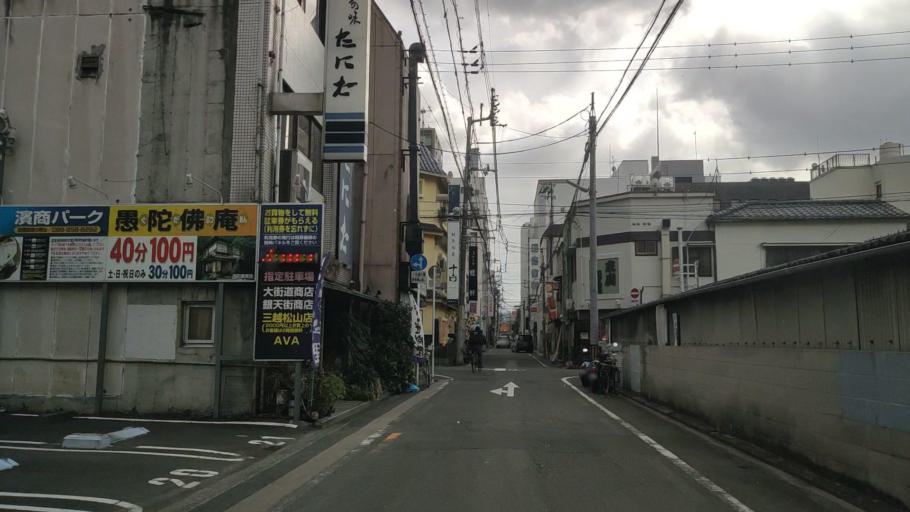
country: JP
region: Ehime
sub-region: Shikoku-chuo Shi
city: Matsuyama
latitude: 33.8395
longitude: 132.7691
